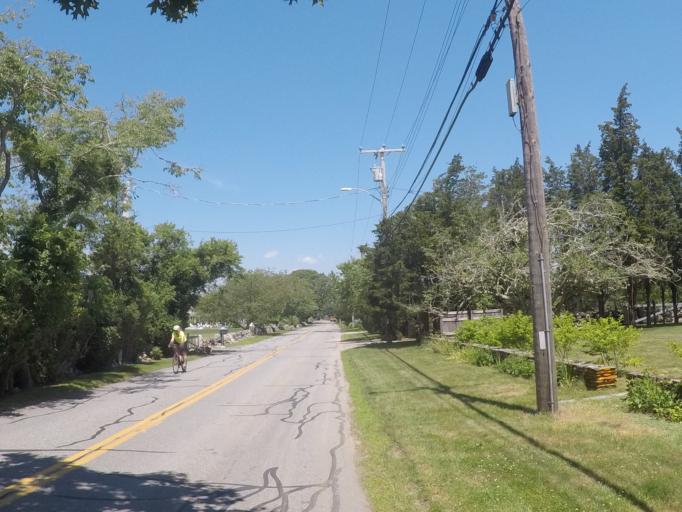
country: US
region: Massachusetts
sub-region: Bristol County
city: Bliss Corner
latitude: 41.5367
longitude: -70.9511
